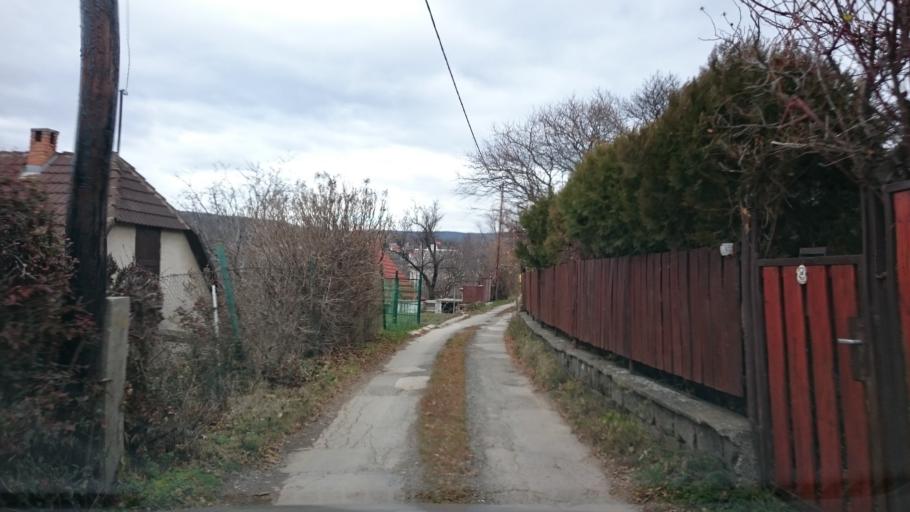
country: HU
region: Baranya
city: Pellerd
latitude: 46.0766
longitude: 18.1785
